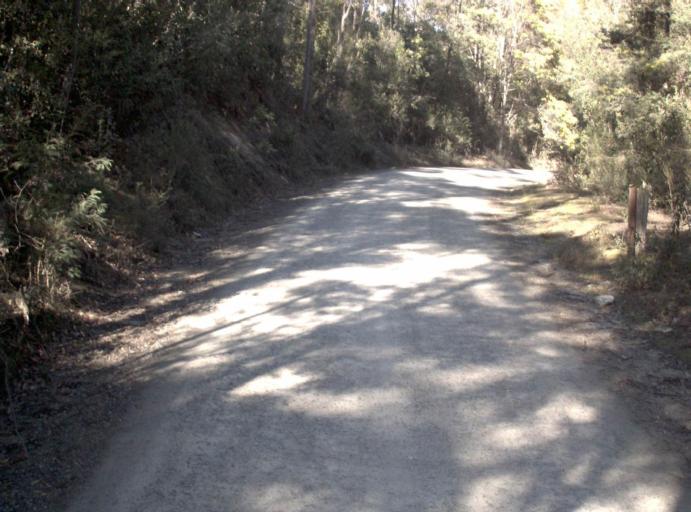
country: AU
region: Tasmania
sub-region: Launceston
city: Mayfield
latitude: -41.1936
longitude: 147.1602
